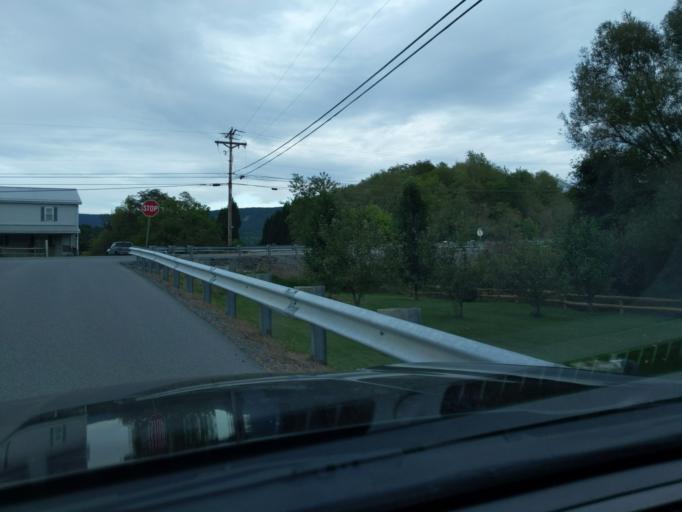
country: US
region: Pennsylvania
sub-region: Blair County
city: Duncansville
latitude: 40.3767
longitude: -78.4331
